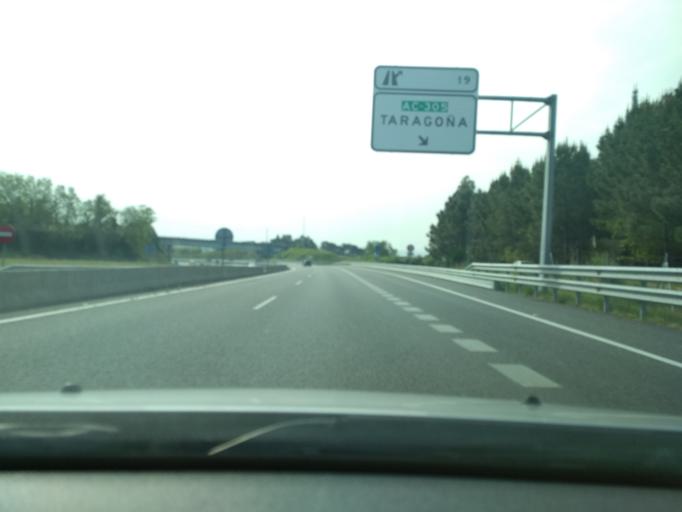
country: ES
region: Galicia
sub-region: Provincia da Coruna
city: Rianxo
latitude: 42.6715
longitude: -8.8292
